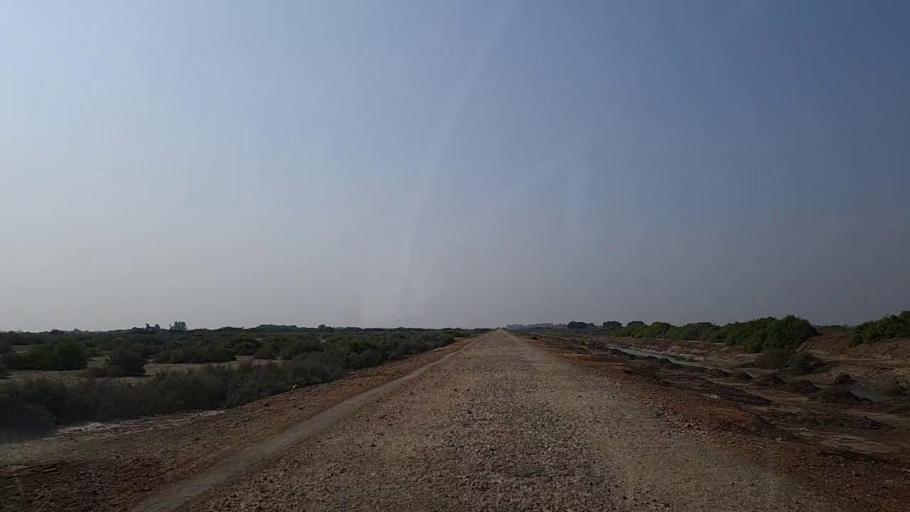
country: PK
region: Sindh
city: Mirpur Sakro
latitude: 24.6344
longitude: 67.7143
